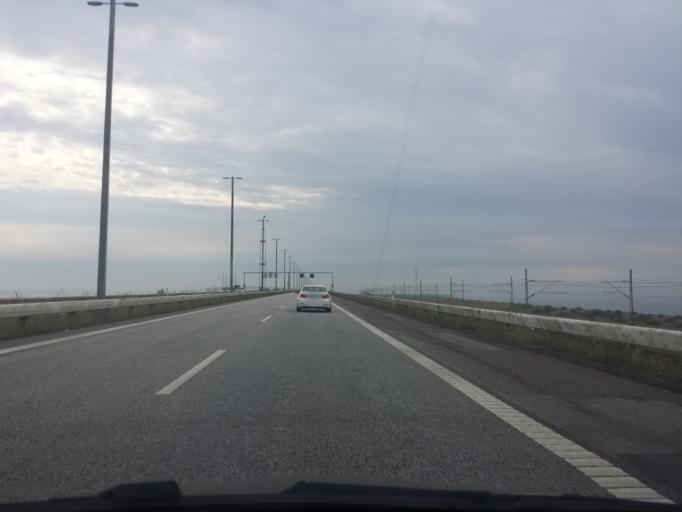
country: DK
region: Capital Region
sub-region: Dragor Kommune
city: Dragor
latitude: 55.6056
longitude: 12.7394
